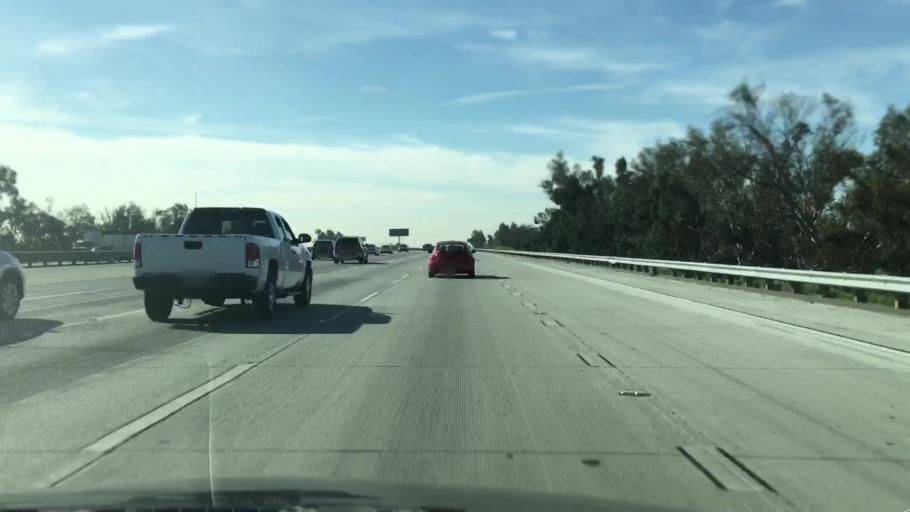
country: US
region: California
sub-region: San Bernardino County
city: Rancho Cucamonga
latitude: 34.1161
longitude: -117.5208
